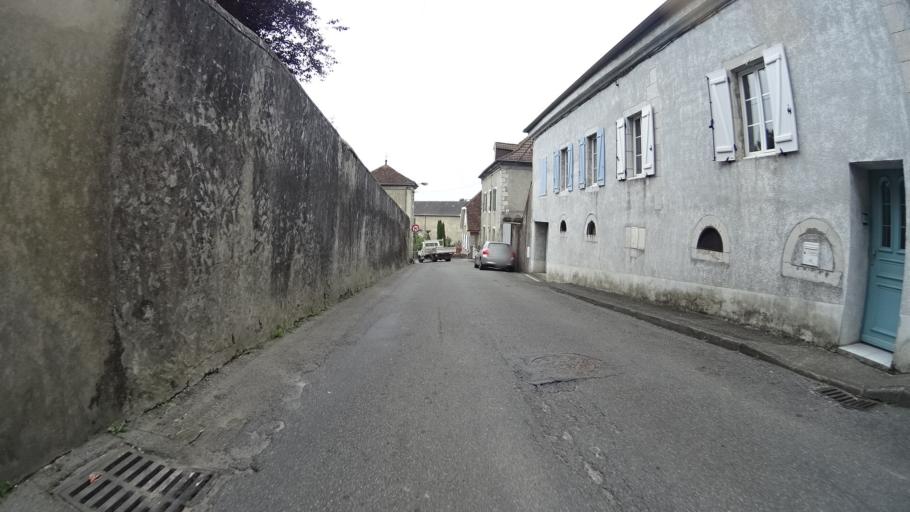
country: FR
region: Aquitaine
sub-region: Departement des Pyrenees-Atlantiques
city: Orthez
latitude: 43.4899
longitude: -0.7730
